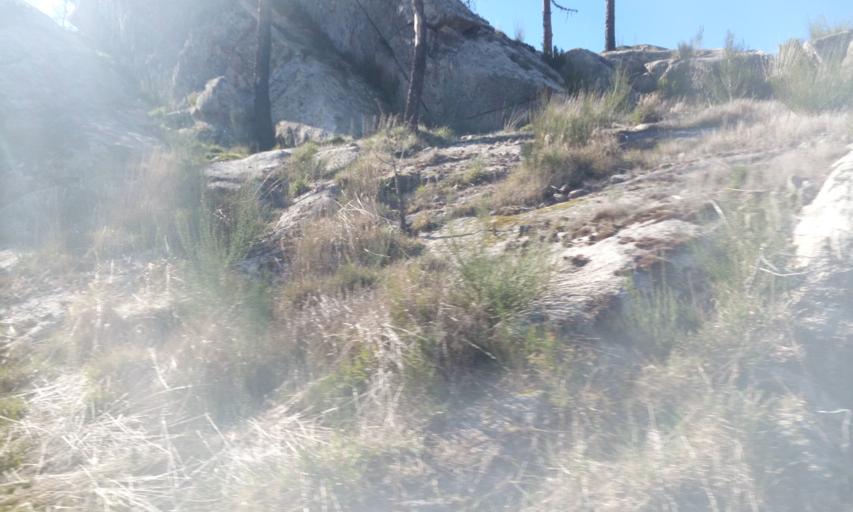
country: PT
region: Guarda
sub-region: Manteigas
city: Manteigas
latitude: 40.4912
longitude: -7.5208
